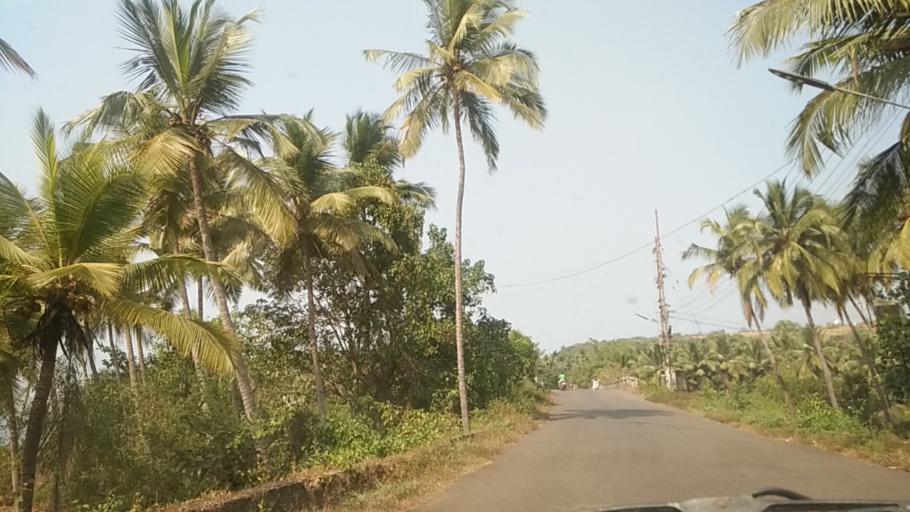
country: IN
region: Goa
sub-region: South Goa
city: Cavelossim
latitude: 15.1364
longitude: 73.9567
